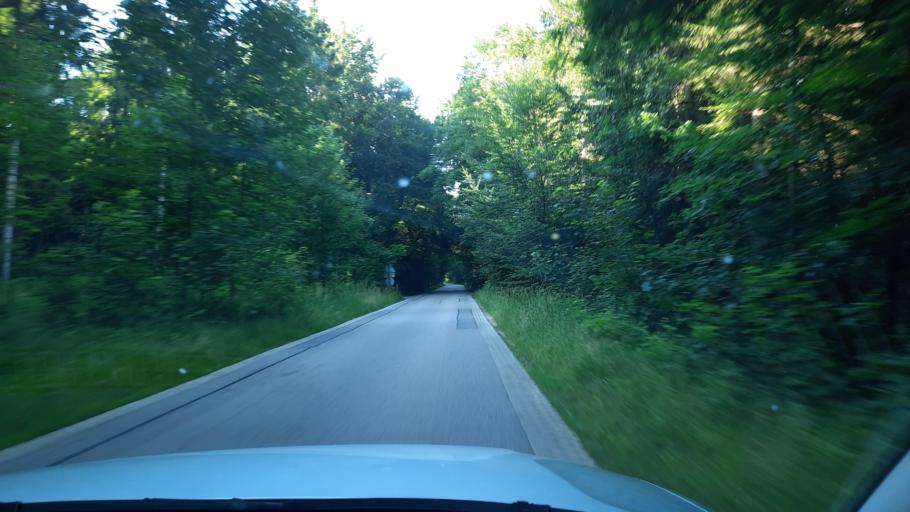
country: DE
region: Bavaria
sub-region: Upper Bavaria
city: Vaterstetten
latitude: 48.0834
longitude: 11.7772
